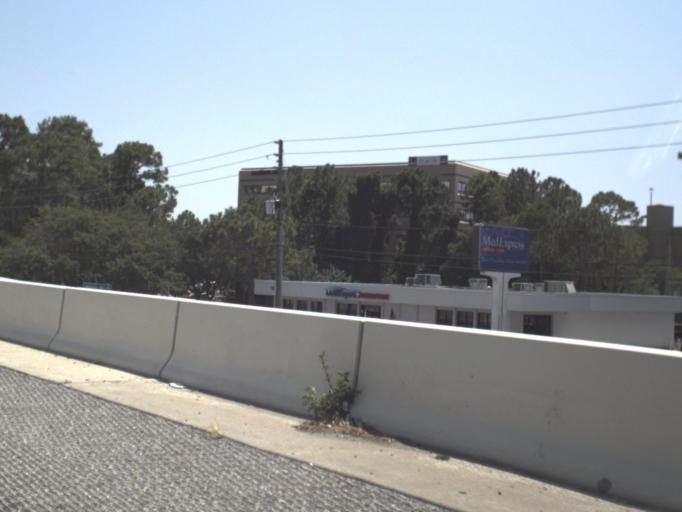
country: US
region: Florida
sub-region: Pinellas County
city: Dunedin
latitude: 28.0166
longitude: -82.7378
